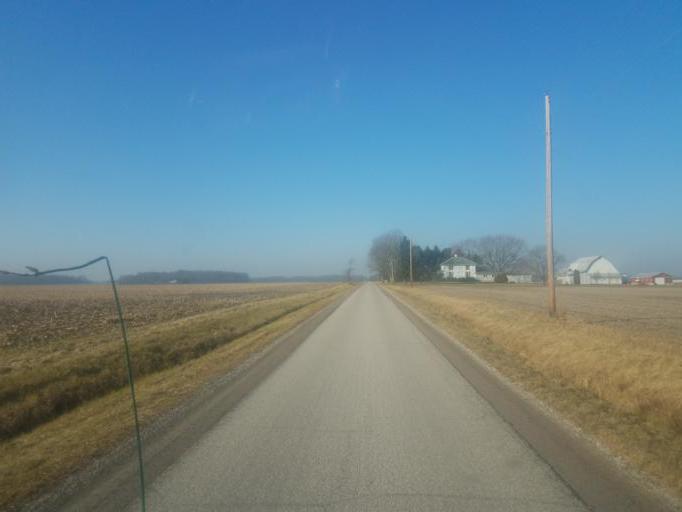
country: US
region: Ohio
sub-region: Huron County
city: Willard
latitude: 41.0373
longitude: -82.9446
